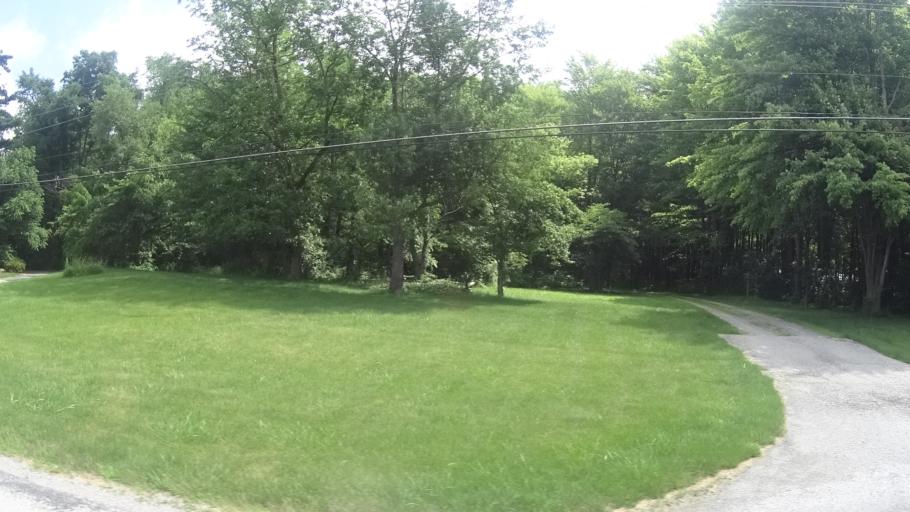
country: US
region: Ohio
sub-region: Huron County
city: Wakeman
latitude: 41.3104
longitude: -82.3636
